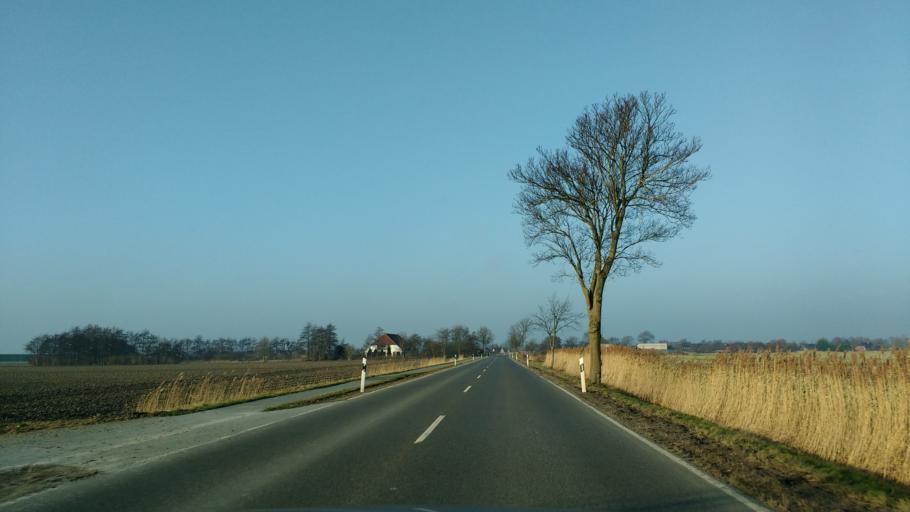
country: DE
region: Schleswig-Holstein
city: Friedrichskoog
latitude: 53.9966
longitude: 8.8925
